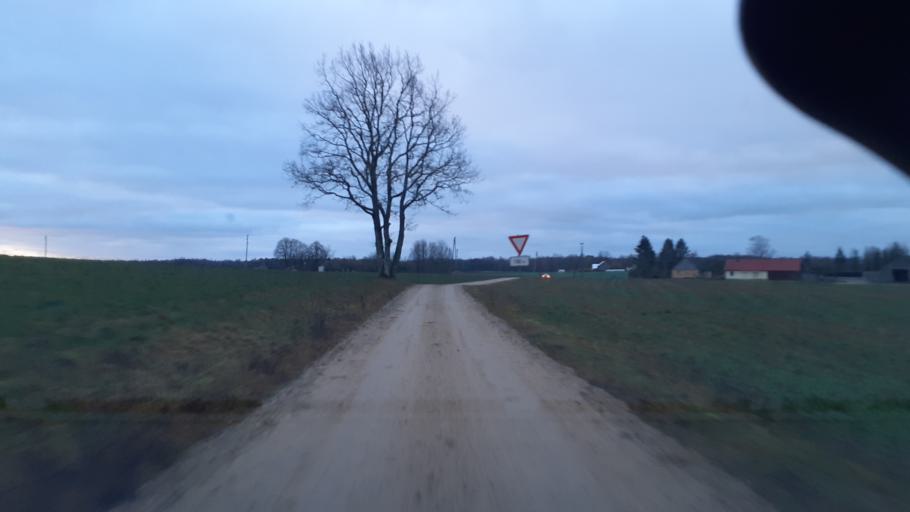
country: LV
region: Alsunga
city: Alsunga
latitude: 56.9057
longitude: 21.7125
